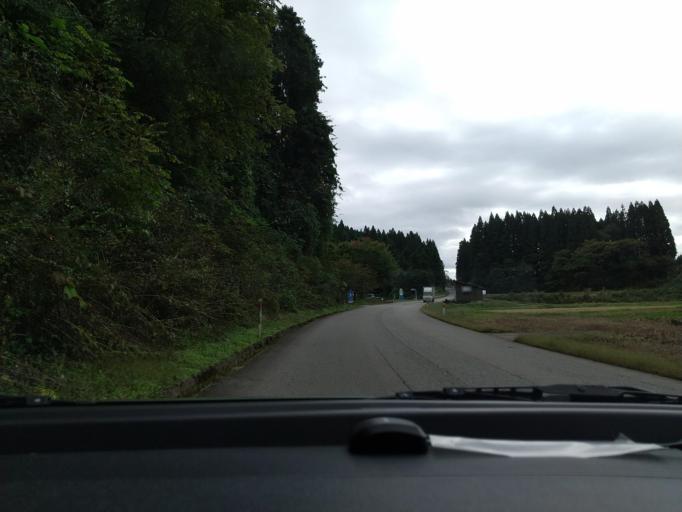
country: JP
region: Akita
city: Kakunodatemachi
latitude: 39.5906
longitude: 140.6197
